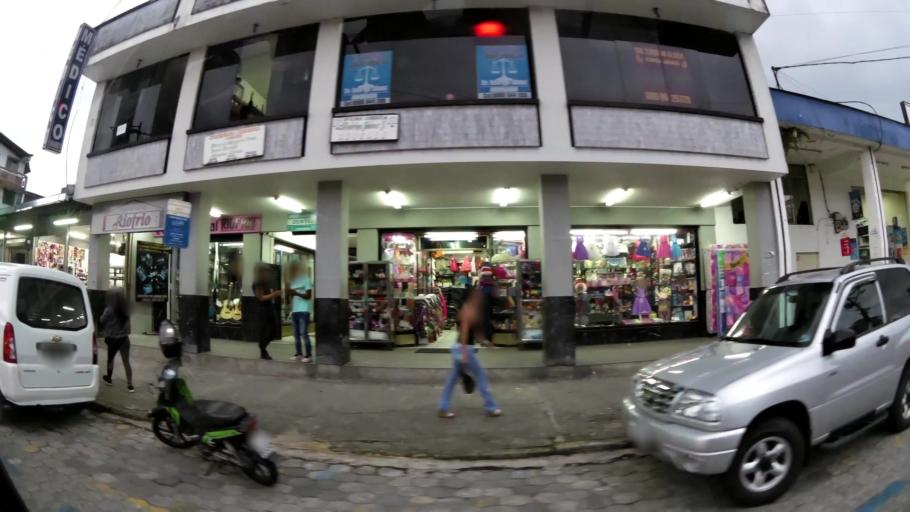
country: EC
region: Pastaza
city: Puyo
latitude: -1.4868
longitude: -77.9988
